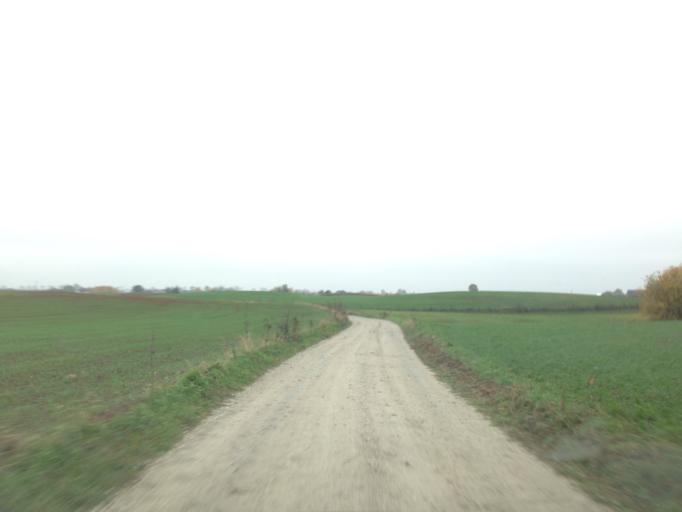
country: PL
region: Kujawsko-Pomorskie
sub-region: Powiat brodnicki
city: Bartniczka
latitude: 53.2203
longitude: 19.6013
